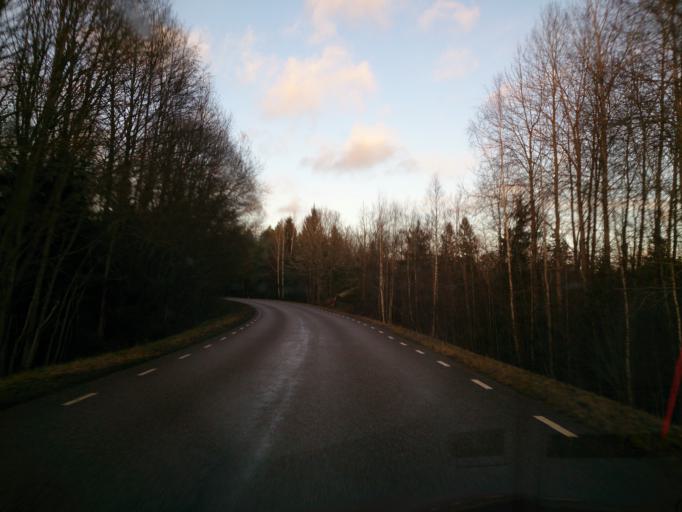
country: SE
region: OEstergoetland
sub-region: Atvidabergs Kommun
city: Atvidaberg
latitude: 58.2337
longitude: 16.0085
